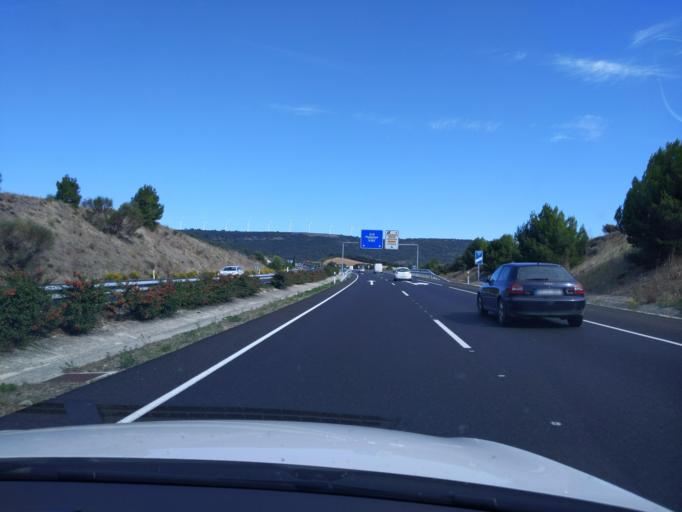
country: ES
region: Navarre
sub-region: Provincia de Navarra
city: Legarda
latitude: 42.7214
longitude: -1.7657
